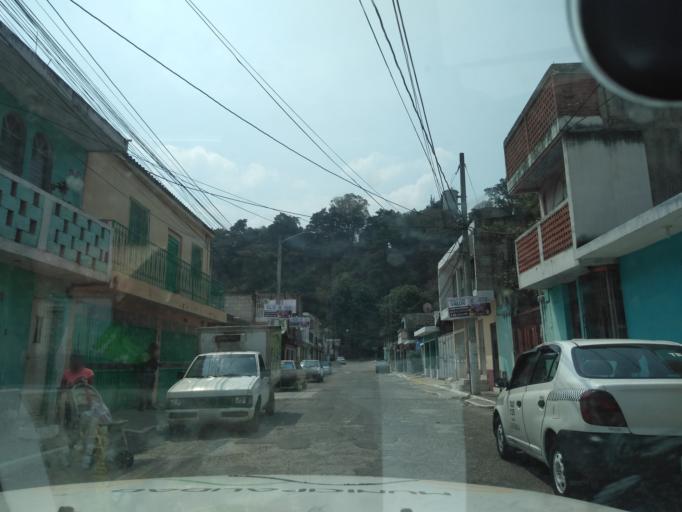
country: GT
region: Guatemala
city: Petapa
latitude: 14.5178
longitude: -90.5418
